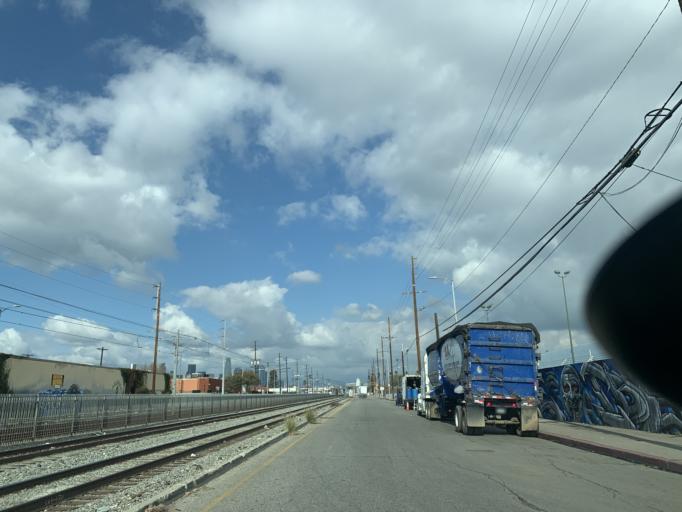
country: US
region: California
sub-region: Los Angeles County
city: Huntington Park
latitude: 34.0112
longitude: -118.2430
